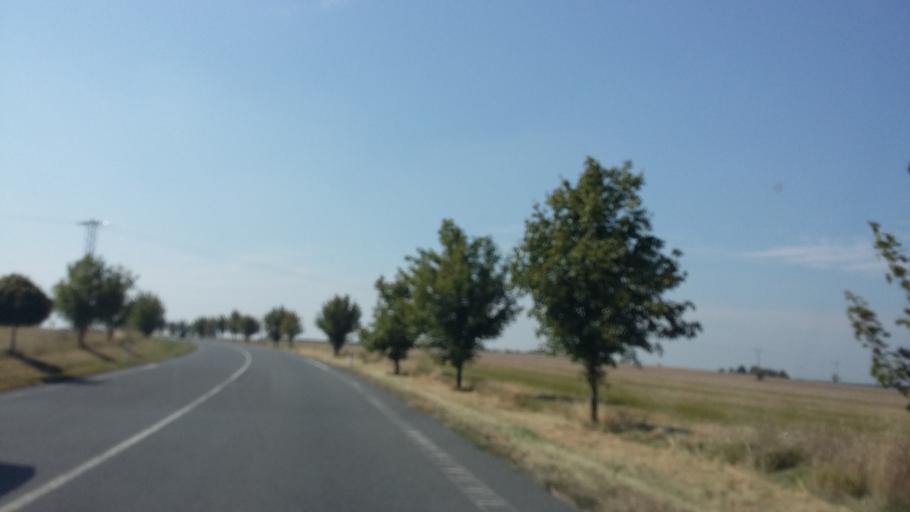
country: CZ
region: Central Bohemia
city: Velky Osek
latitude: 50.0938
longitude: 15.2572
